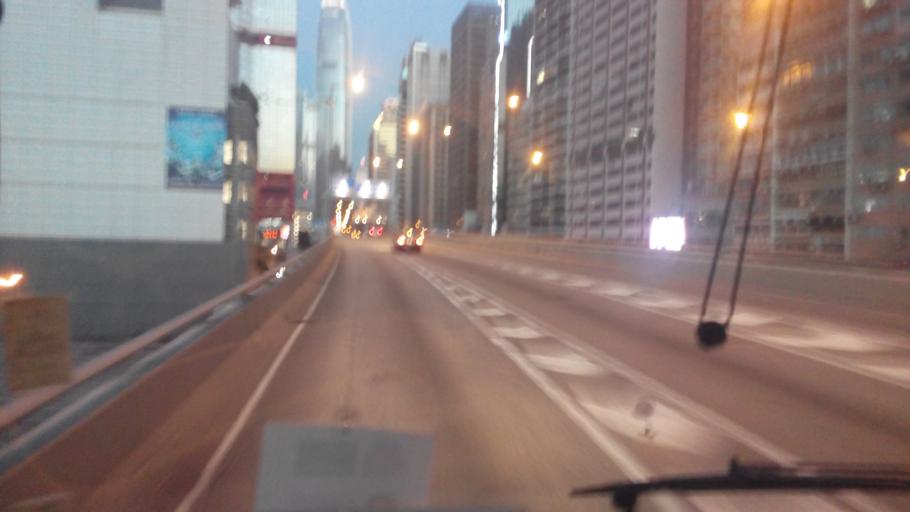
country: HK
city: Hong Kong
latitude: 22.2887
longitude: 114.1478
